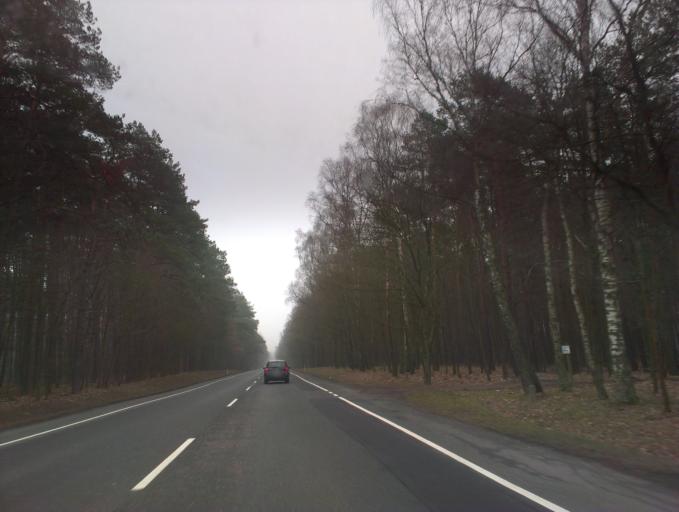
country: PL
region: Greater Poland Voivodeship
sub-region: Powiat pilski
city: Ujscie
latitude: 53.0232
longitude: 16.8127
